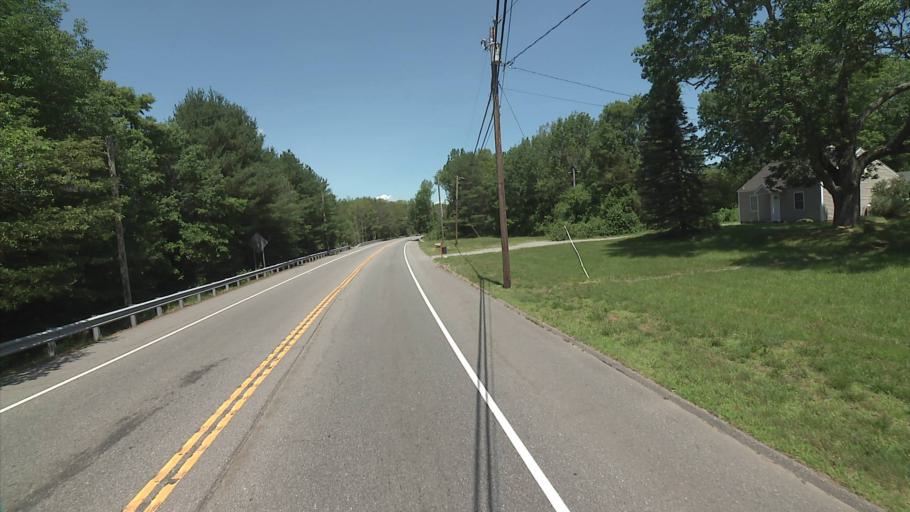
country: US
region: Connecticut
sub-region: New London County
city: Old Mystic
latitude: 41.4541
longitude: -71.9058
